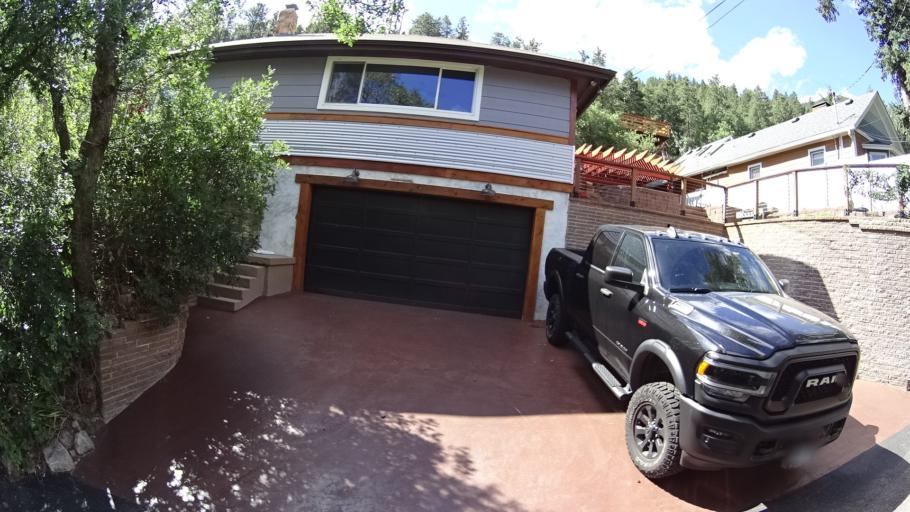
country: US
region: Colorado
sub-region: El Paso County
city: Manitou Springs
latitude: 38.8562
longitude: -104.9288
